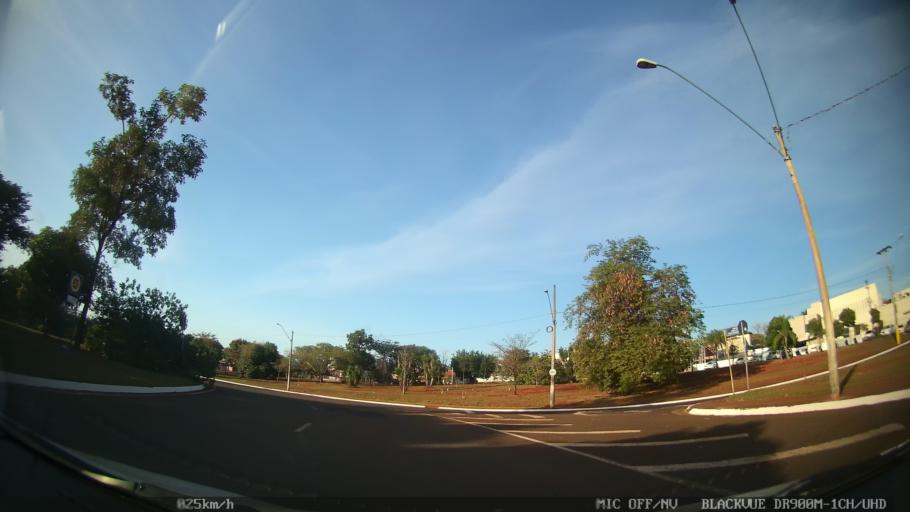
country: BR
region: Sao Paulo
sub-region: Ribeirao Preto
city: Ribeirao Preto
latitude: -21.2156
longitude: -47.7815
